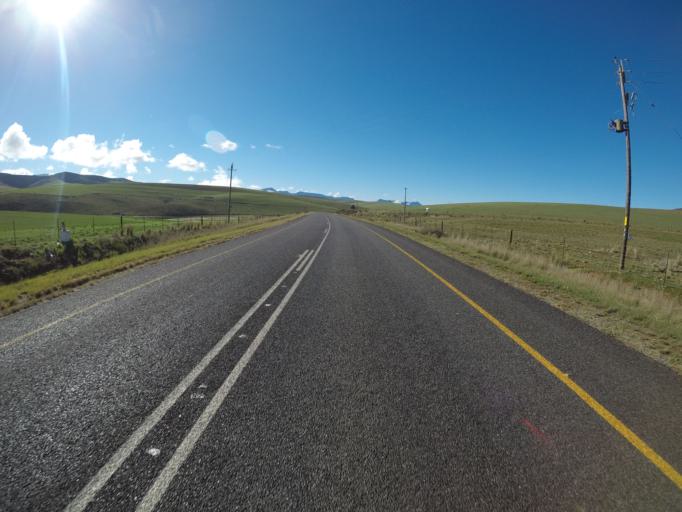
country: ZA
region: Western Cape
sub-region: Overberg District Municipality
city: Caledon
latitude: -34.1542
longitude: 19.4712
